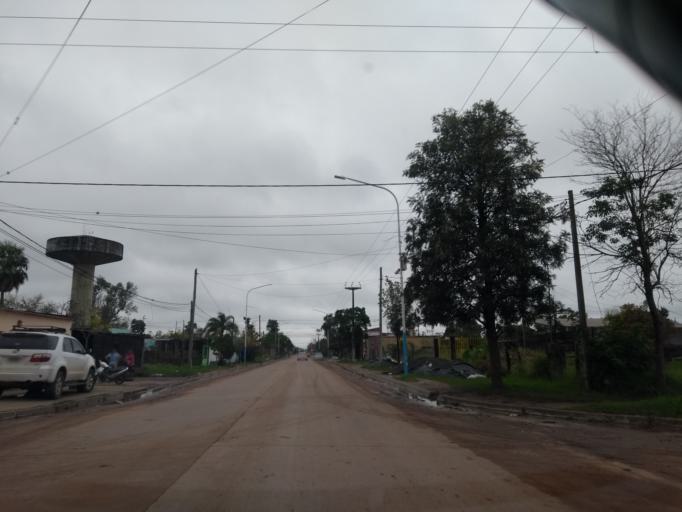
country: AR
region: Chaco
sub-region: Departamento de Quitilipi
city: Quitilipi
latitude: -26.8755
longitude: -60.2192
